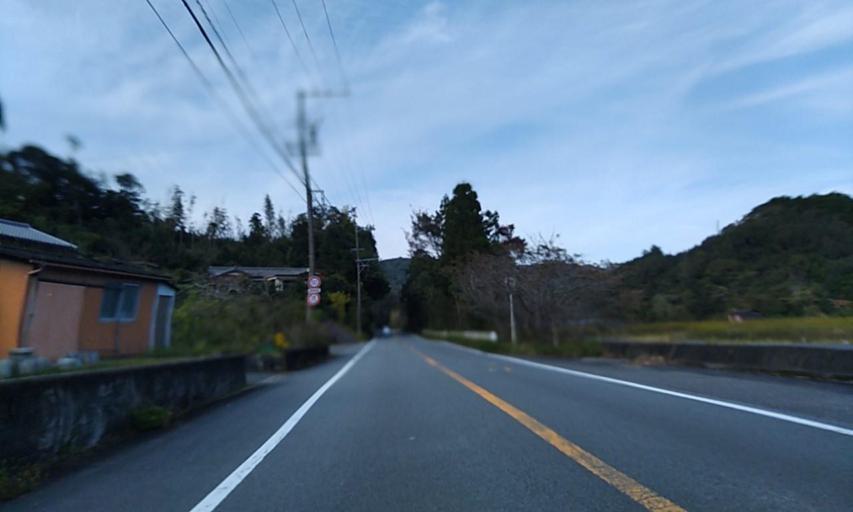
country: JP
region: Mie
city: Ise
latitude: 34.3457
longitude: 136.7318
